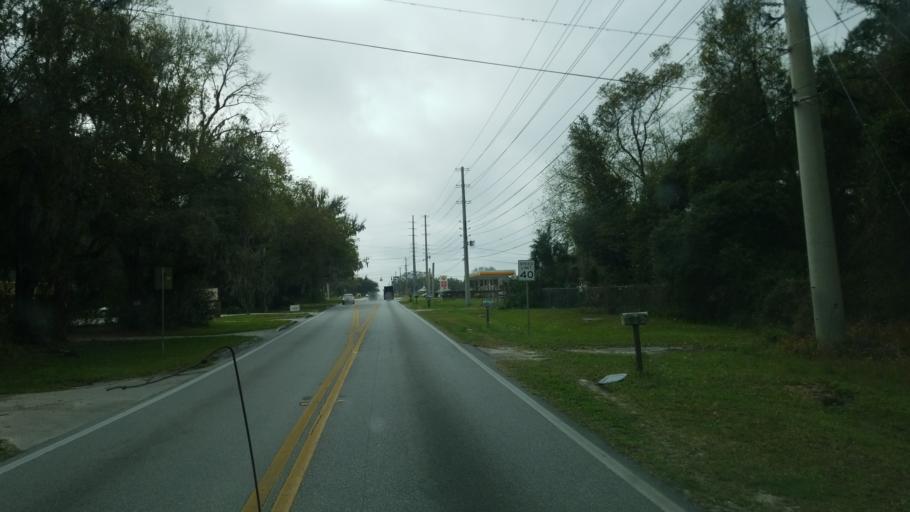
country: US
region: Florida
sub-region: Polk County
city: Kathleen
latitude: 28.0824
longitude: -82.0068
